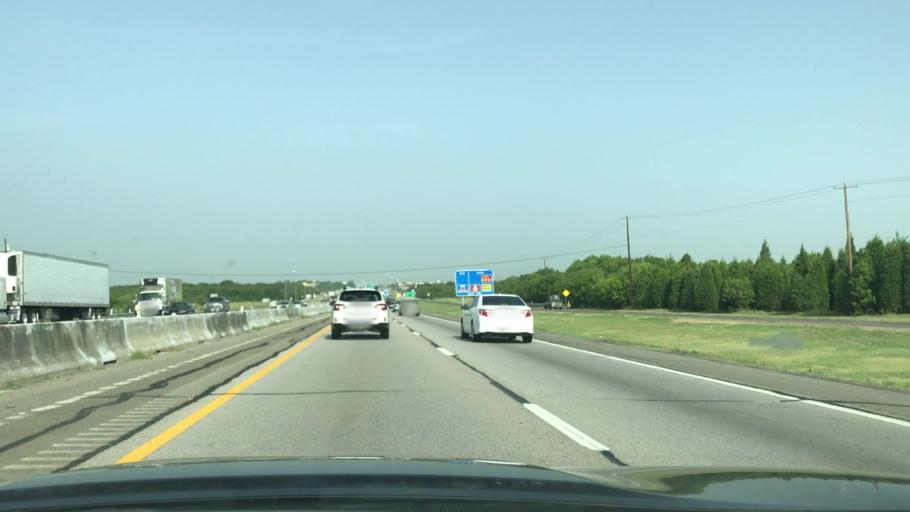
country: US
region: Texas
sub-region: Dallas County
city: Sunnyvale
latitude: 32.7885
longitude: -96.5833
